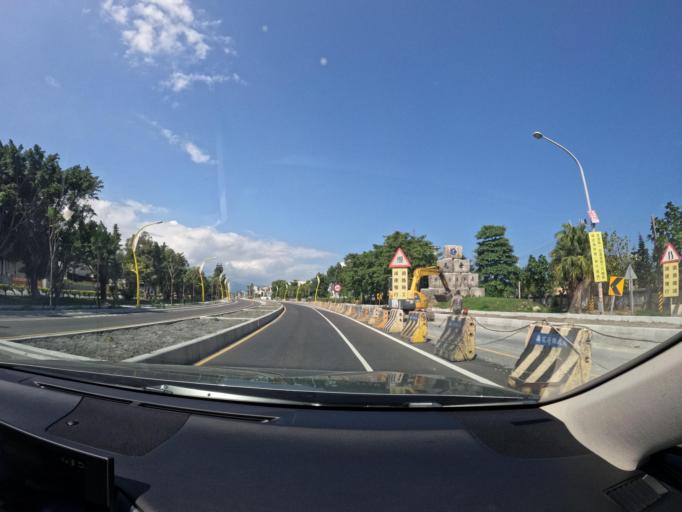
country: TW
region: Taiwan
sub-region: Hualien
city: Hualian
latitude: 23.9319
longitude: 121.5946
